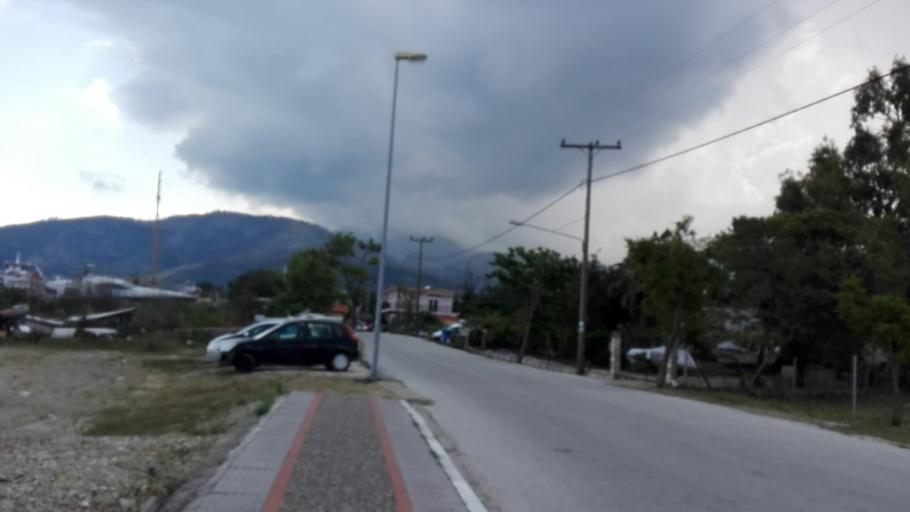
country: GR
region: East Macedonia and Thrace
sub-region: Nomos Kavalas
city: Prinos
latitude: 40.7595
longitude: 24.5729
